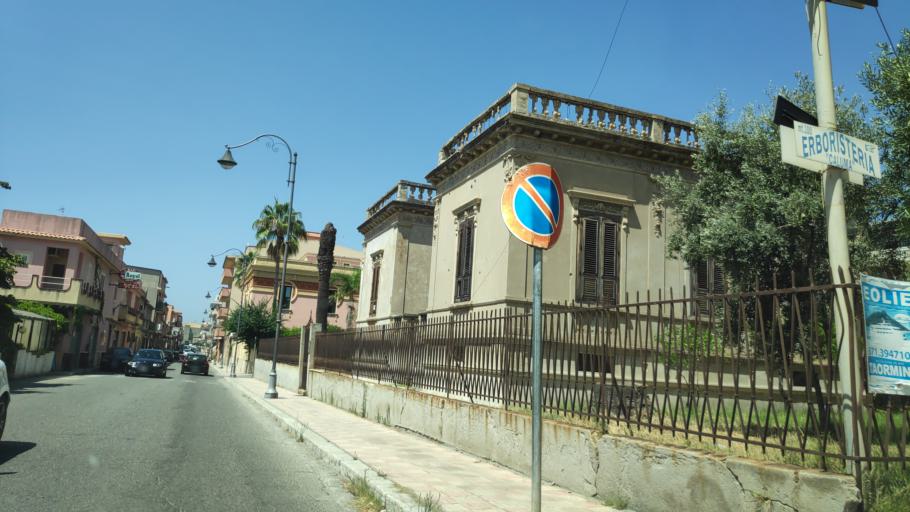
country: IT
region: Calabria
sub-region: Provincia di Reggio Calabria
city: Bova Marina
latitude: 37.9305
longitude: 15.9198
